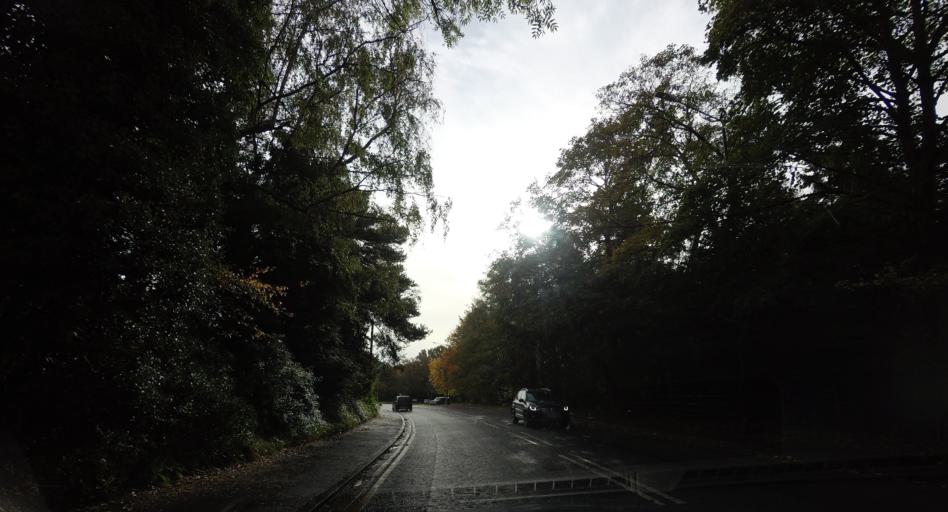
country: GB
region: England
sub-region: Kent
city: Sevenoaks
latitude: 51.2800
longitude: 0.1726
